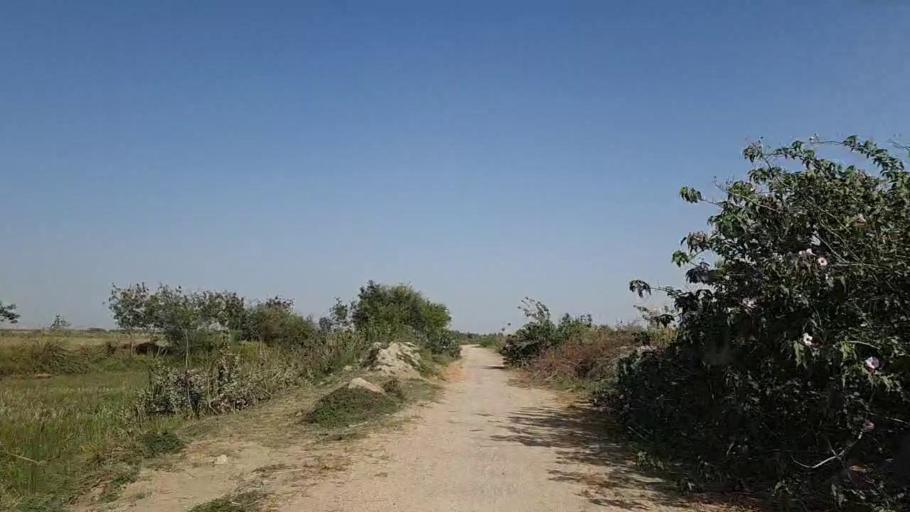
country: PK
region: Sindh
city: Chuhar Jamali
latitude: 24.4814
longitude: 68.1110
